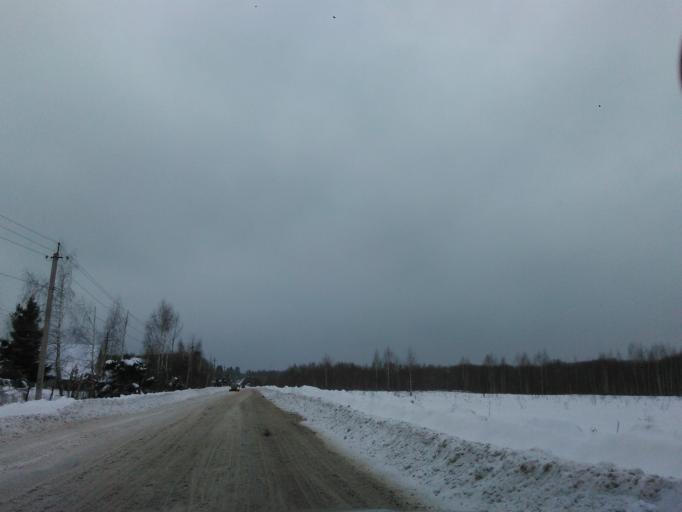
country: RU
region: Moskovskaya
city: Yakhroma
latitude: 56.2637
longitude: 37.4388
